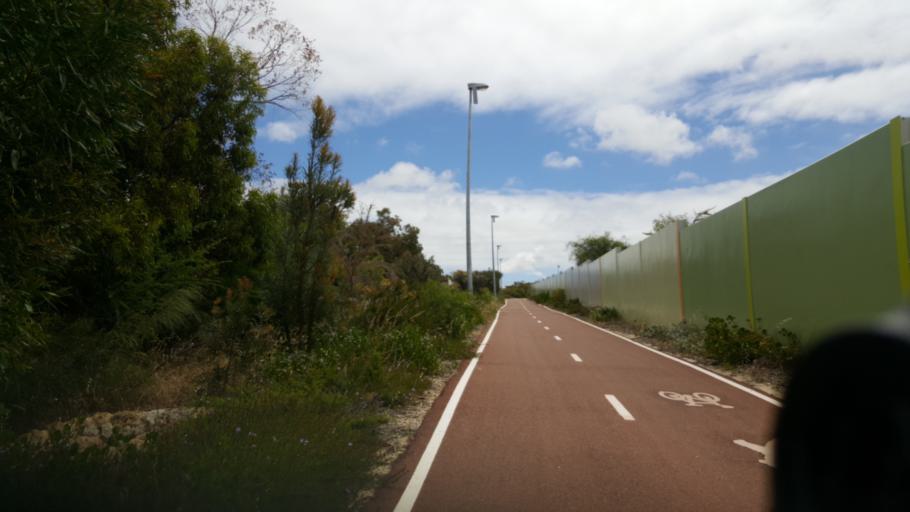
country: AU
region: Western Australia
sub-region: Bayswater
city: Embleton
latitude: -31.8685
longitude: 115.8906
